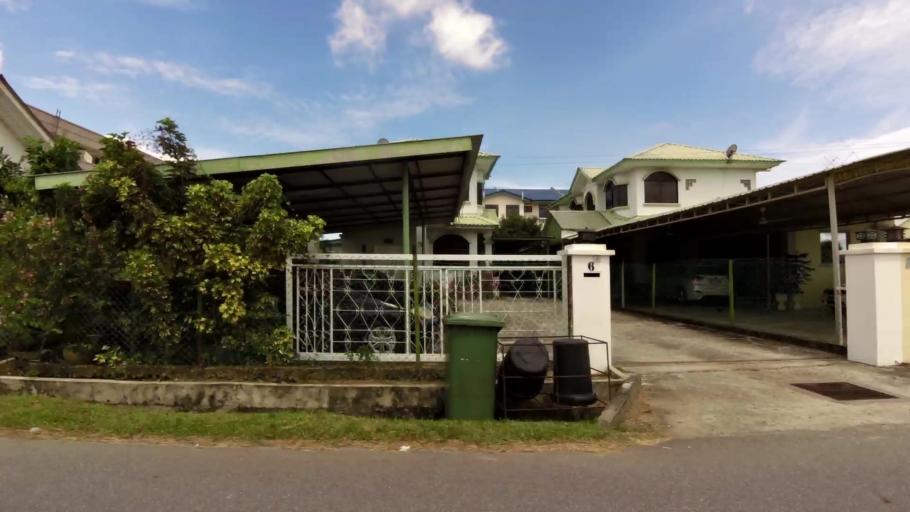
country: BN
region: Brunei and Muara
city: Bandar Seri Begawan
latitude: 4.9424
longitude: 114.9060
